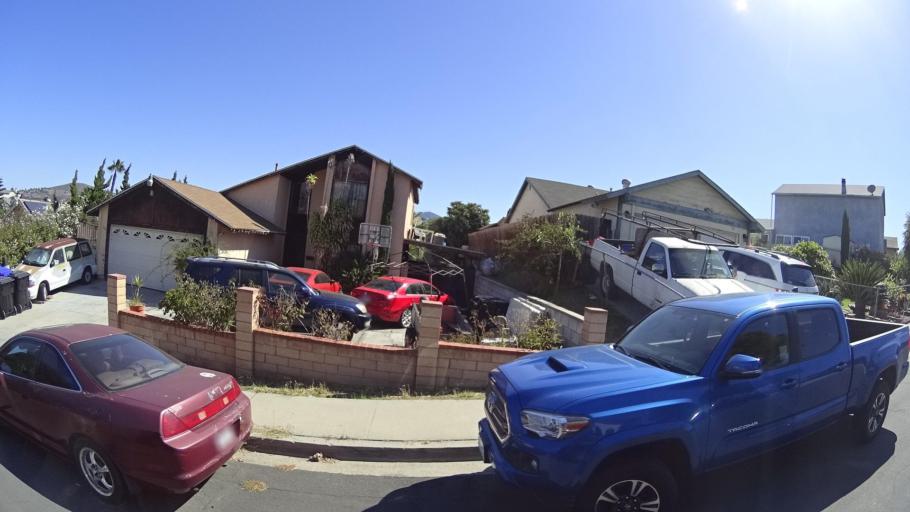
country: US
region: California
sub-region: San Diego County
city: La Presa
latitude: 32.7034
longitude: -117.0227
